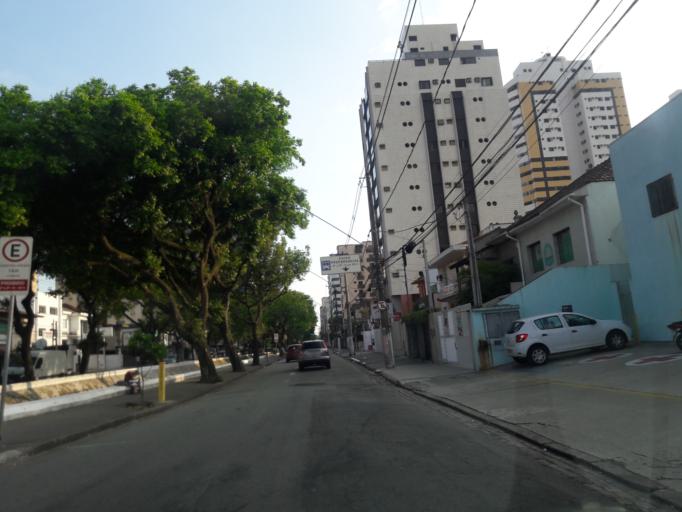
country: BR
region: Sao Paulo
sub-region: Santos
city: Santos
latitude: -23.9619
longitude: -46.3385
